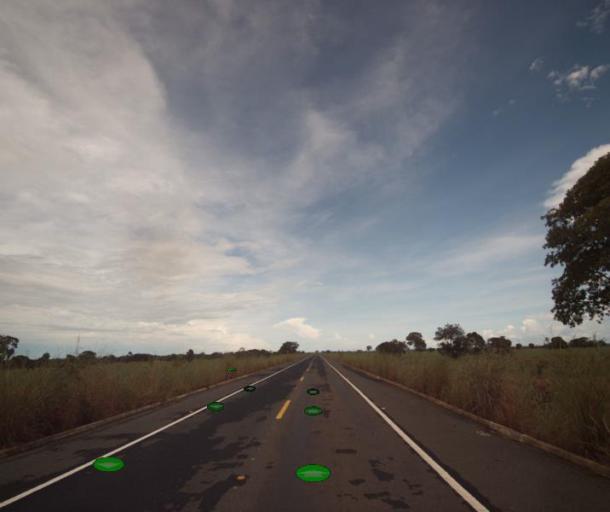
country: BR
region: Goias
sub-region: Sao Miguel Do Araguaia
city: Sao Miguel do Araguaia
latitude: -13.2802
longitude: -50.4957
